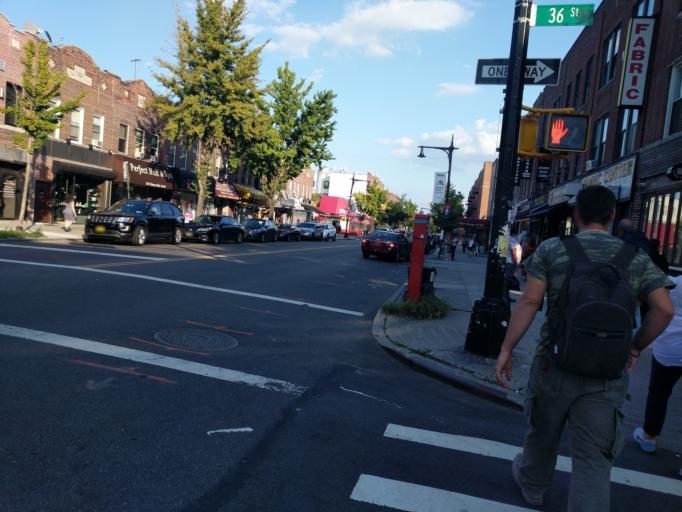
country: US
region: New York
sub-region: Queens County
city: Long Island City
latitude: 40.7743
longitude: -73.9083
